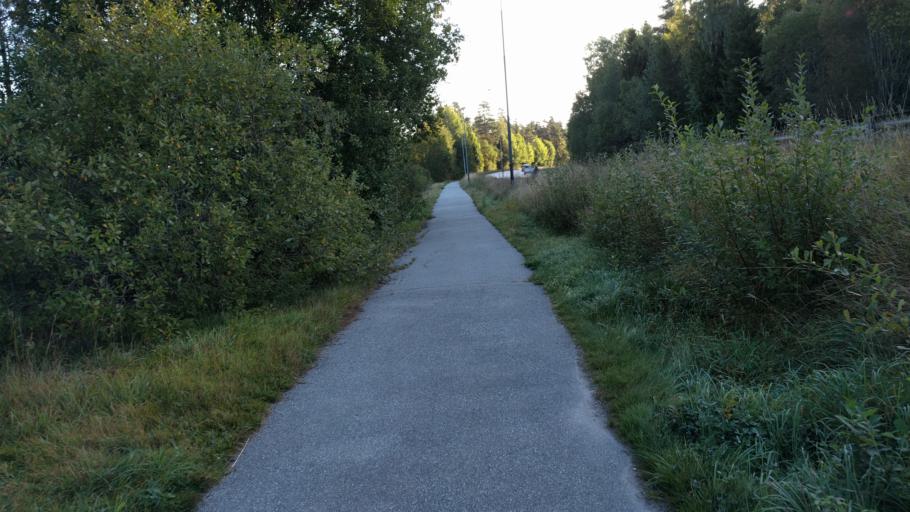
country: SE
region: Stockholm
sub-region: Taby Kommun
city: Taby
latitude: 59.4702
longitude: 18.0834
